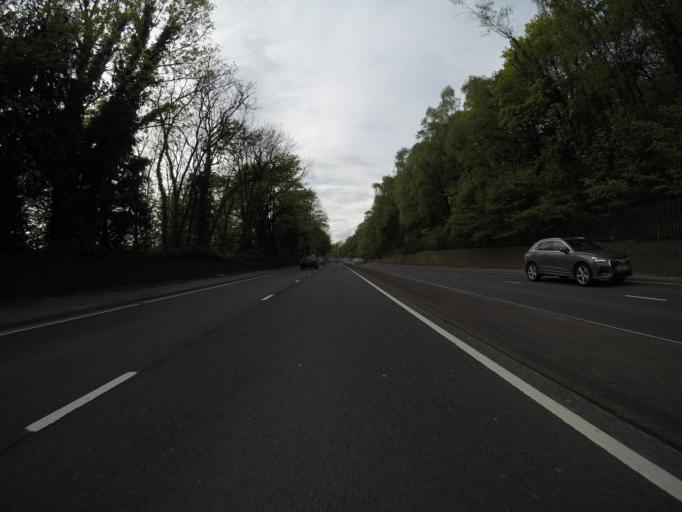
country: GB
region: Scotland
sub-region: West Dunbartonshire
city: Dumbarton
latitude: 55.9396
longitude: -4.5366
